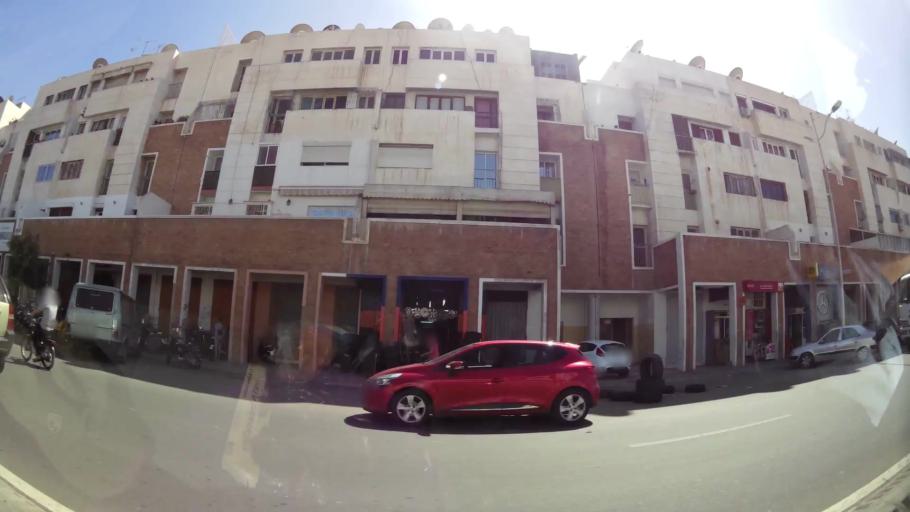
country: MA
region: Oued ed Dahab-Lagouira
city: Dakhla
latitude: 30.4163
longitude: -9.5726
